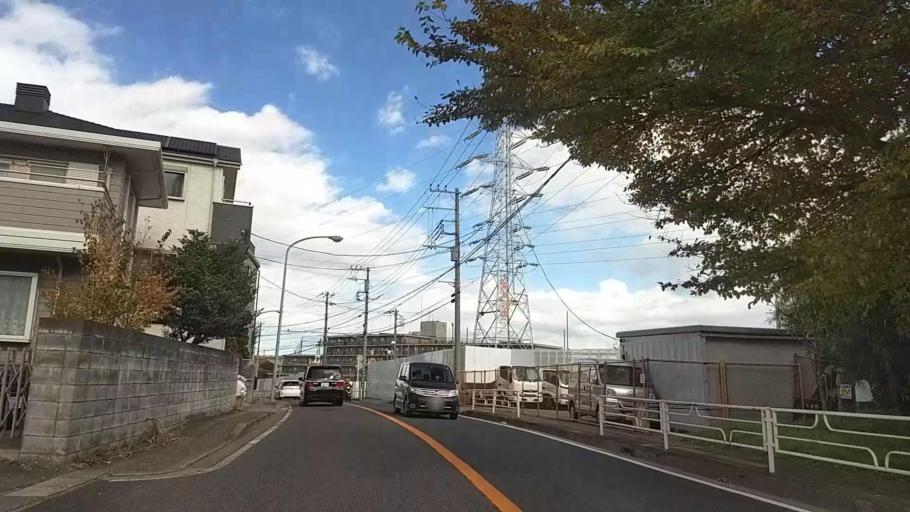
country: JP
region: Kanagawa
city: Yokohama
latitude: 35.5065
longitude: 139.6392
